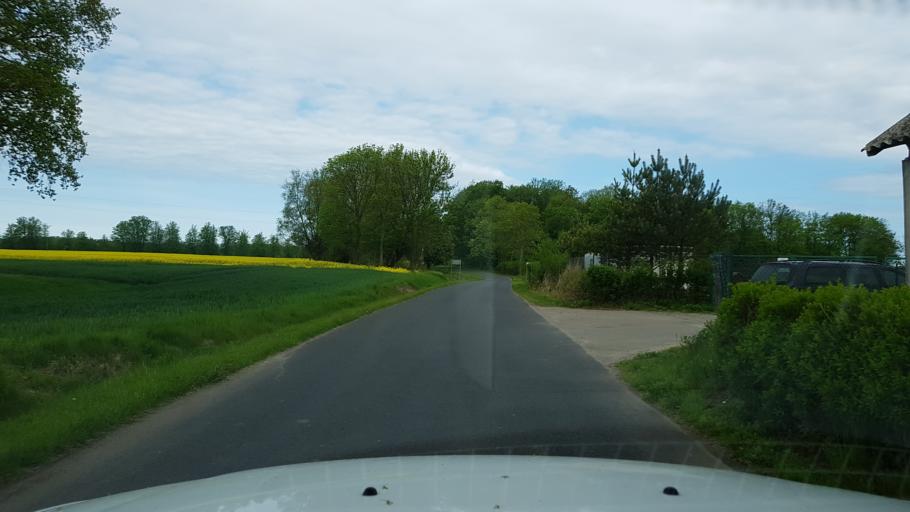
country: PL
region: West Pomeranian Voivodeship
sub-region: Powiat kolobrzeski
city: Ustronie Morskie
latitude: 54.2209
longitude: 15.8048
